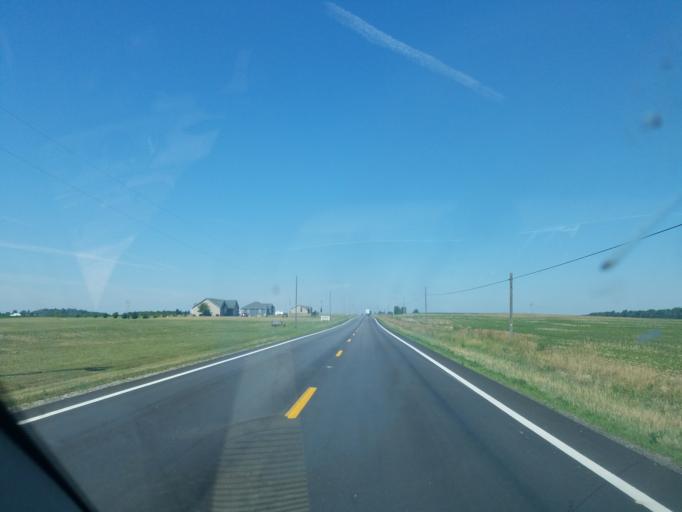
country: US
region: Ohio
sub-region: Shelby County
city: Jackson Center
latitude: 40.4394
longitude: -84.1025
